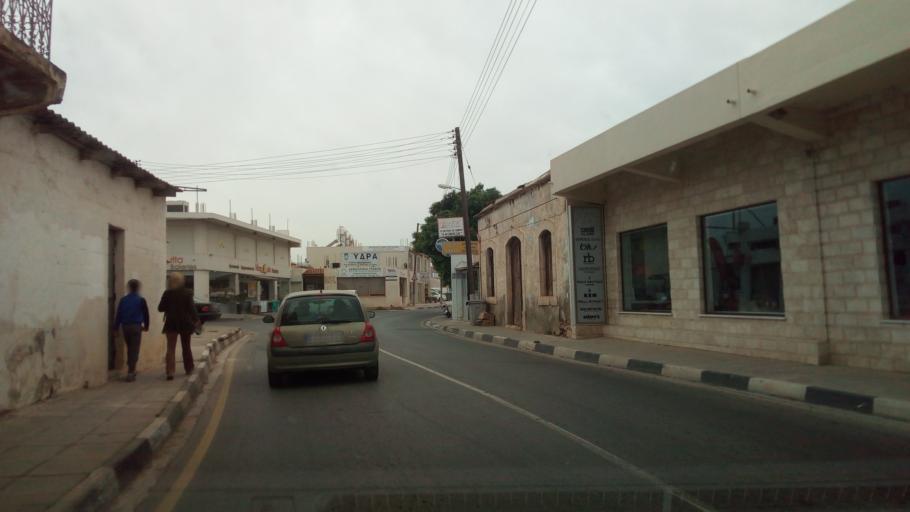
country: CY
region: Ammochostos
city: Liopetri
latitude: 34.9775
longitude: 33.8501
